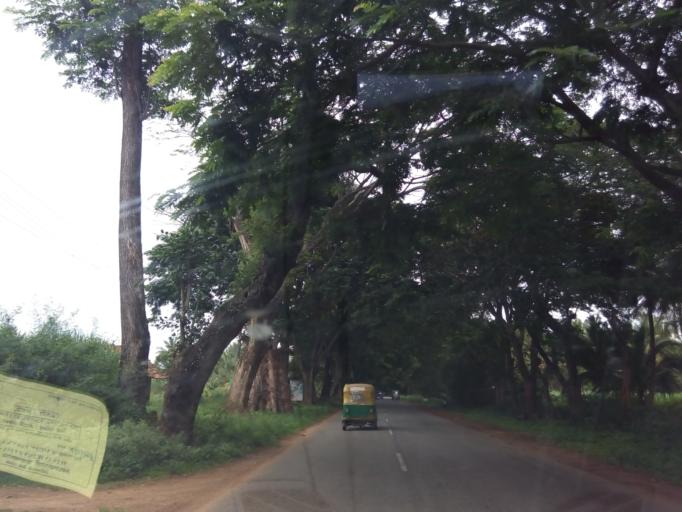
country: IN
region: Karnataka
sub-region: Hassan
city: Channarayapatna
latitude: 12.8764
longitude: 76.4298
